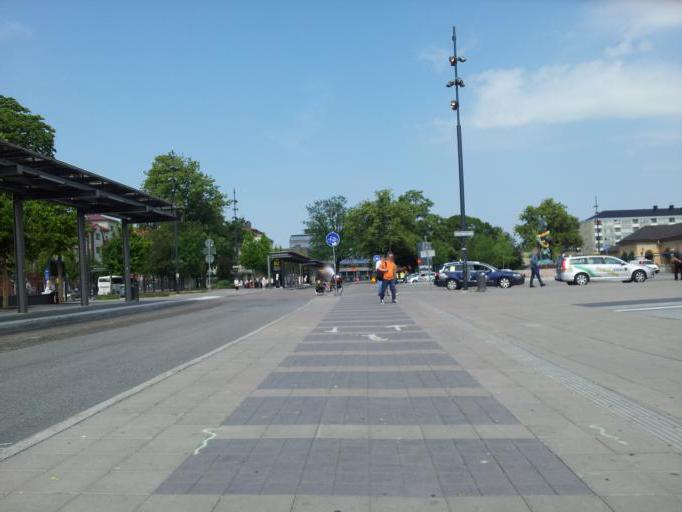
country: SE
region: Uppsala
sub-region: Uppsala Kommun
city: Uppsala
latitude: 59.8579
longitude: 17.6461
